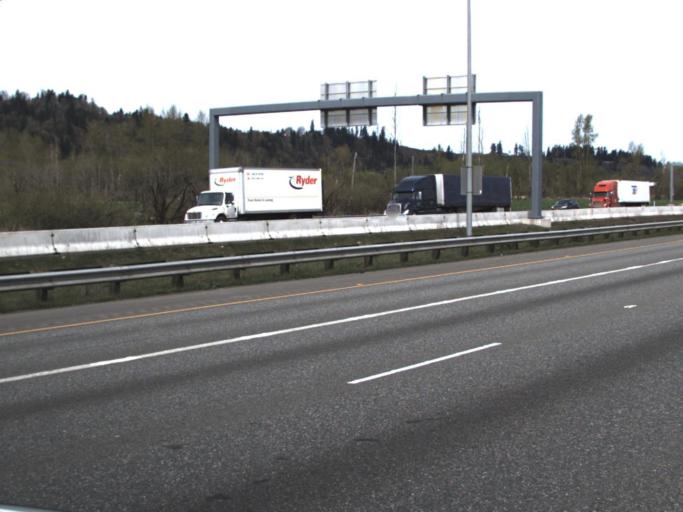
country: US
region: Washington
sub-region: King County
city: Auburn
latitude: 47.3143
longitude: -122.2452
